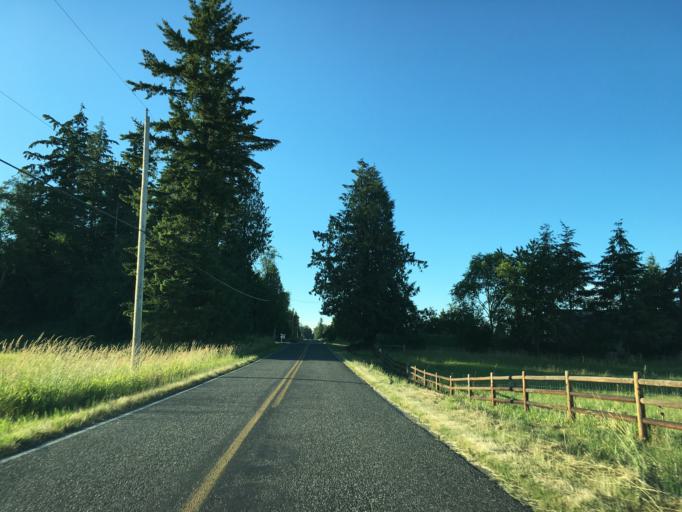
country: US
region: Washington
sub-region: Whatcom County
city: Lynden
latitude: 48.9805
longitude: -122.5297
